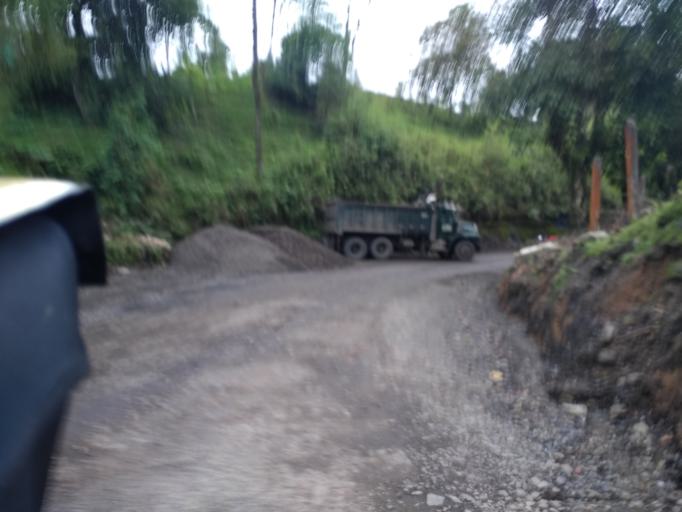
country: CO
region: Santander
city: Landazuri
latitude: 6.1836
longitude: -73.7184
